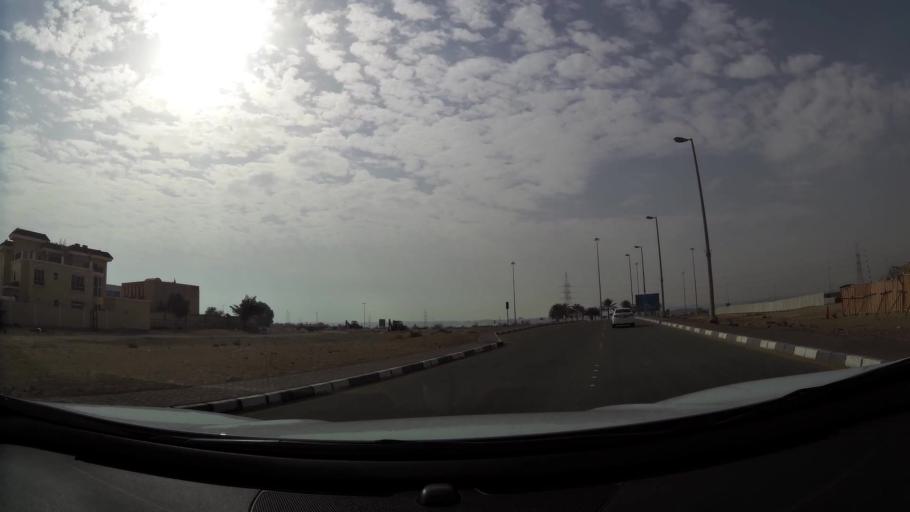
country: AE
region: Abu Dhabi
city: Abu Dhabi
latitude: 24.2577
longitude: 54.7104
